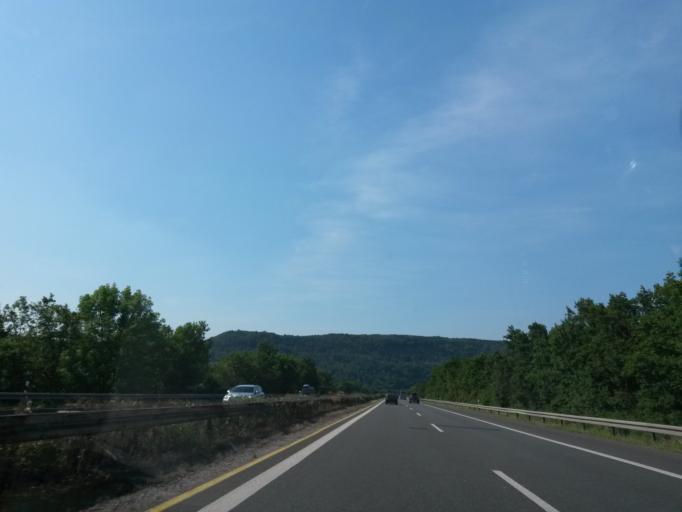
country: DE
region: Bavaria
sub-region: Regierungsbezirk Unterfranken
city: Elfershausen
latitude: 50.1326
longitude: 9.9547
